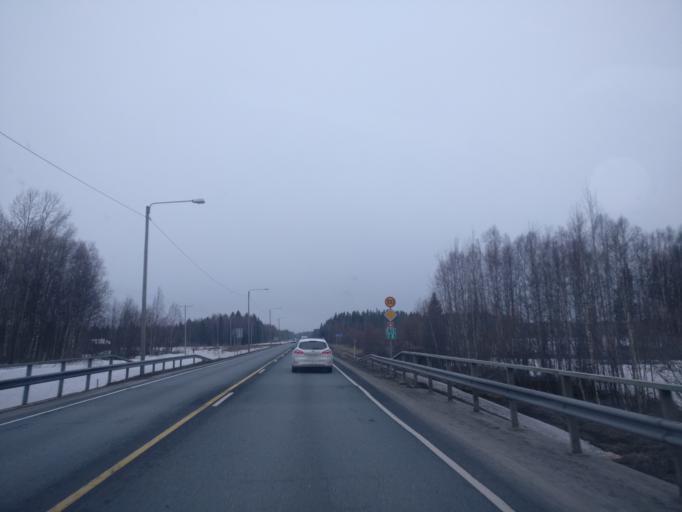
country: FI
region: Lapland
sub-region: Kemi-Tornio
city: Simo
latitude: 65.6700
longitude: 24.9254
